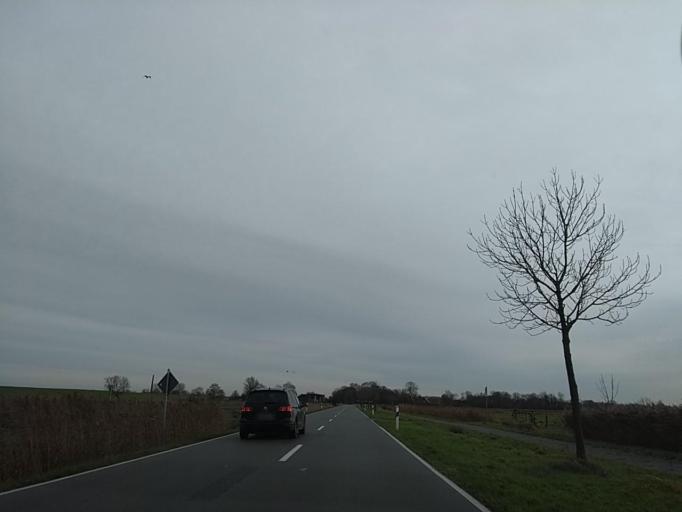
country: DE
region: Lower Saxony
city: Jemgum
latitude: 53.2893
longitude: 7.3618
